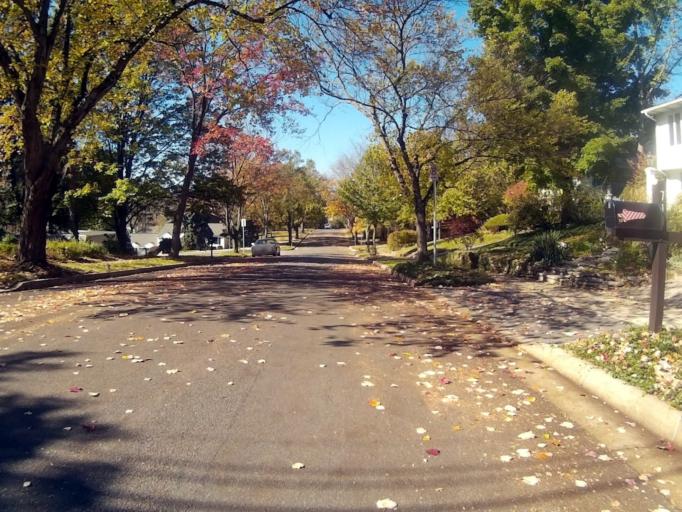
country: US
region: Pennsylvania
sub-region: Centre County
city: State College
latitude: 40.7929
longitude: -77.8799
